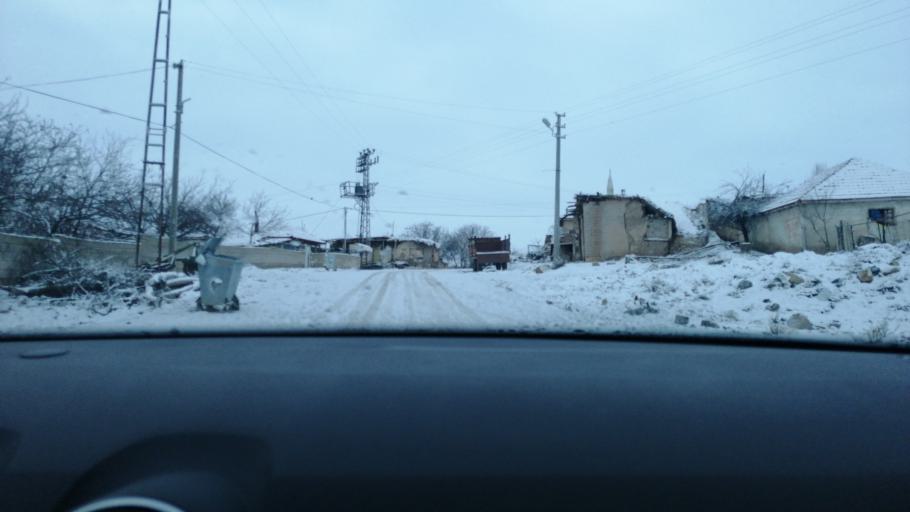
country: TR
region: Aksaray
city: Agacoren
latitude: 38.9351
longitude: 33.9487
